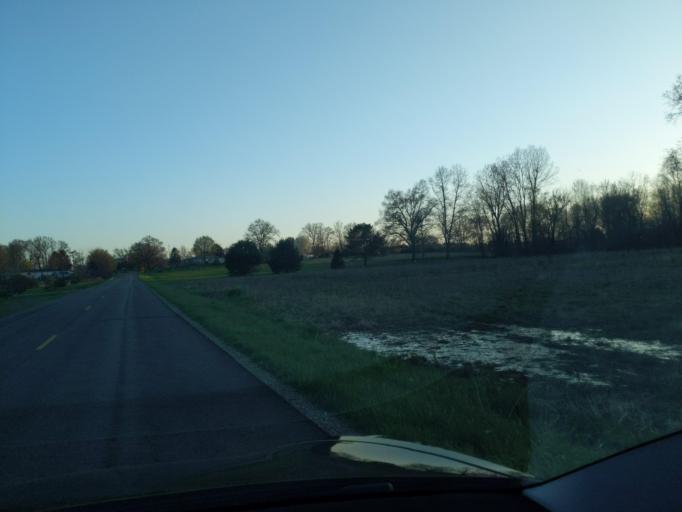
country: US
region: Michigan
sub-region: Ingham County
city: Stockbridge
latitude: 42.4923
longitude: -84.2895
